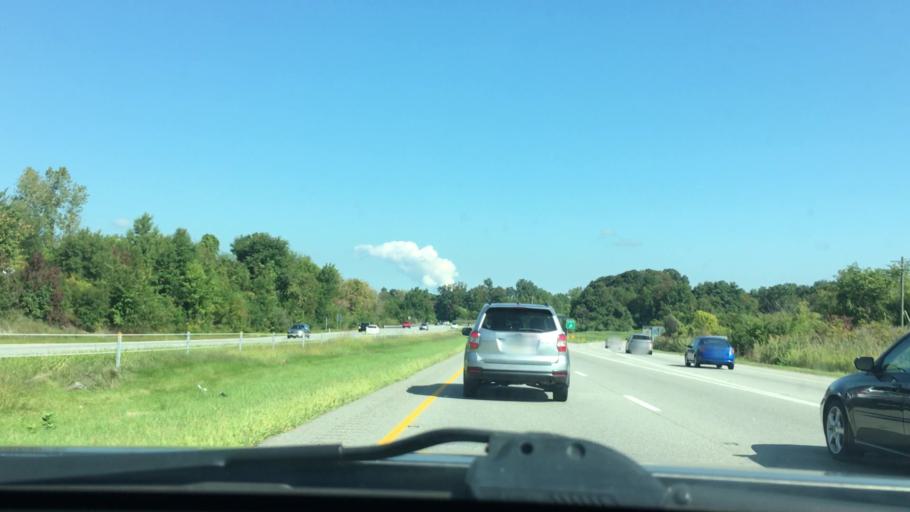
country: US
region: Pennsylvania
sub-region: Chester County
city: West Chester
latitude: 39.9865
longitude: -75.5896
